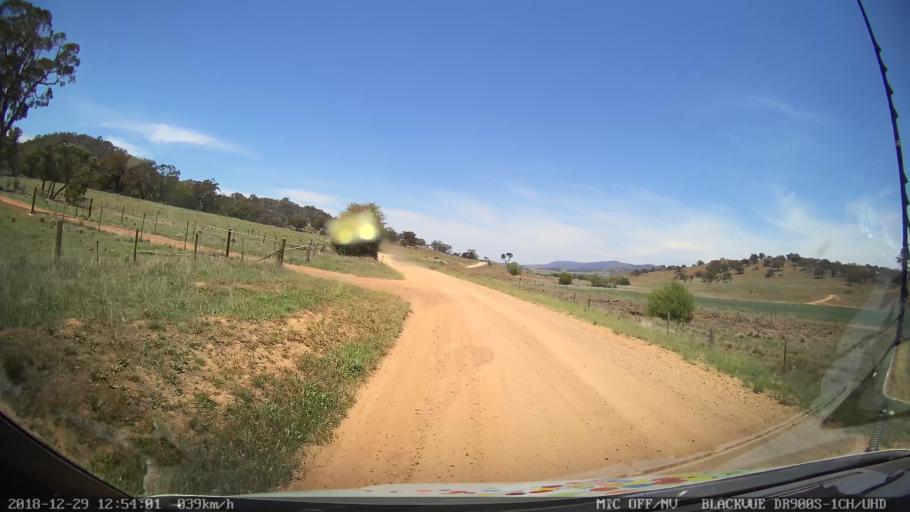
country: AU
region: Australian Capital Territory
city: Macarthur
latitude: -35.6889
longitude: 149.1877
